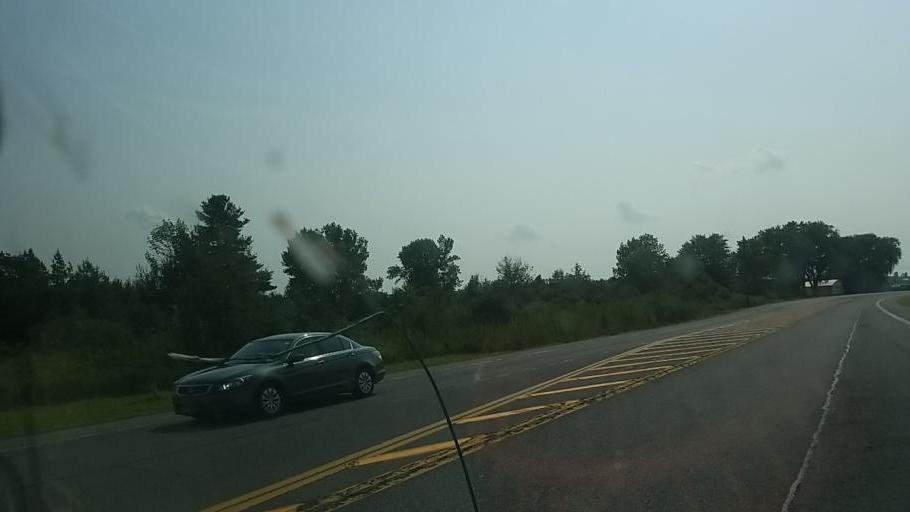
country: US
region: New York
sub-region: Montgomery County
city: Amsterdam
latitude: 42.9349
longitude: -74.2342
